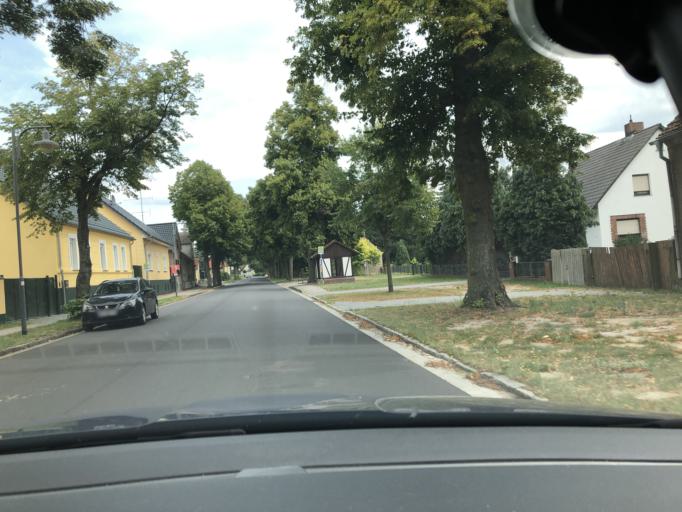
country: DE
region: Brandenburg
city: Schlepzig
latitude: 52.0322
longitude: 13.8315
